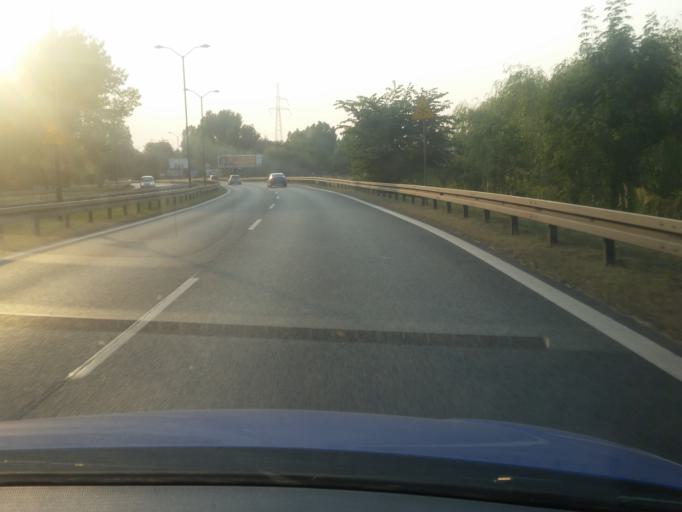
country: PL
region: Silesian Voivodeship
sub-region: Katowice
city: Katowice
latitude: 50.2624
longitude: 19.0616
